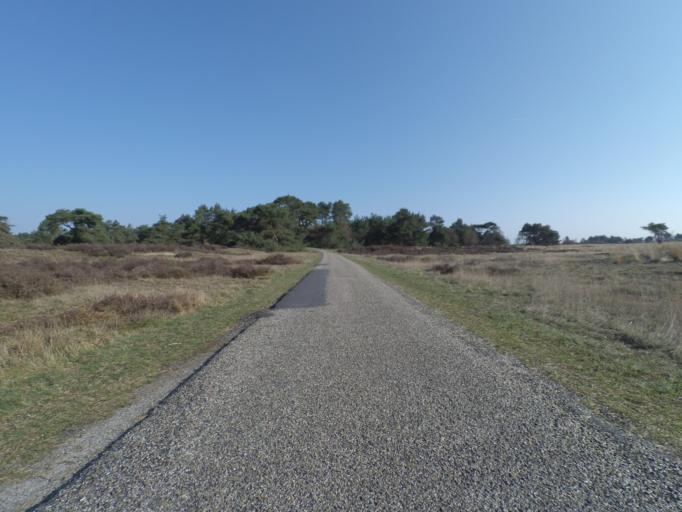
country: NL
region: Gelderland
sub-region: Gemeente Ede
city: Otterlo
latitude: 52.0903
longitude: 5.8518
